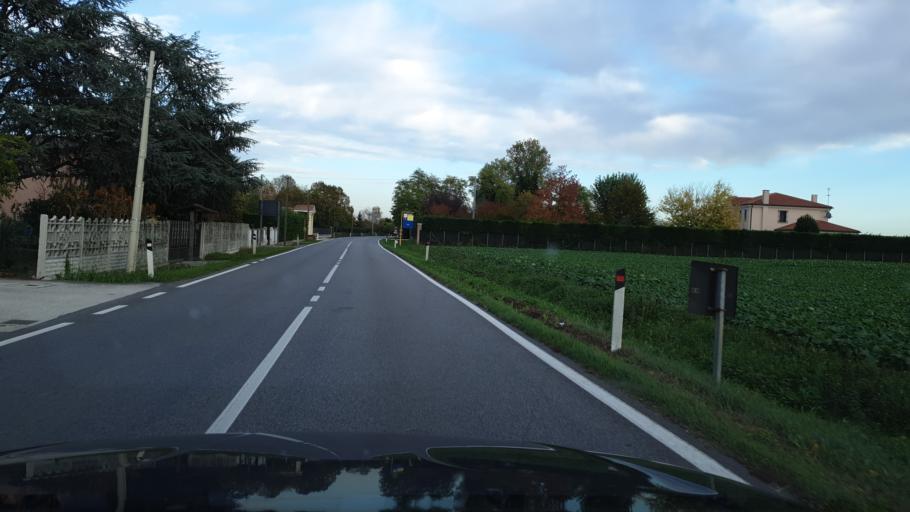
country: IT
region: Veneto
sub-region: Provincia di Padova
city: San Pietro Viminario
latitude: 45.2258
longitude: 11.8200
